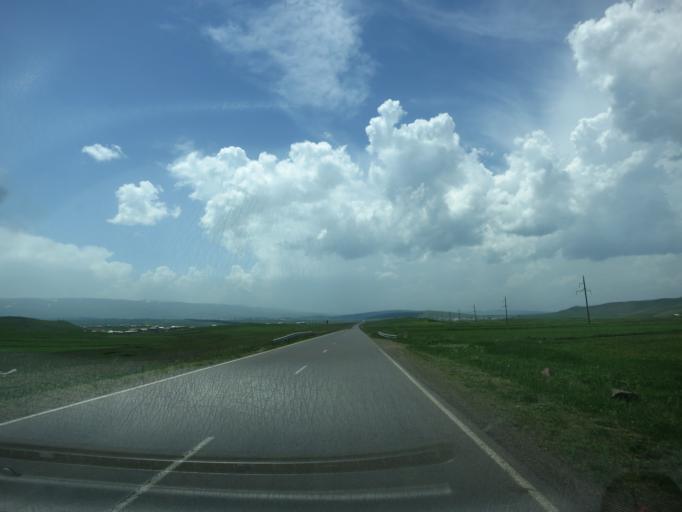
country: GE
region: Samtskhe-Javakheti
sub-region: Ninotsminda
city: Ninotsminda
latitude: 41.2967
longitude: 43.6714
